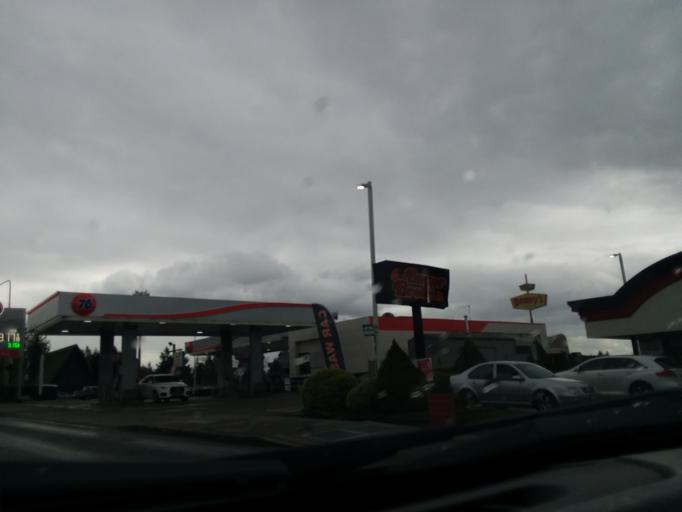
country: US
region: Washington
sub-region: King County
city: Burien
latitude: 47.4704
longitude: -122.3348
